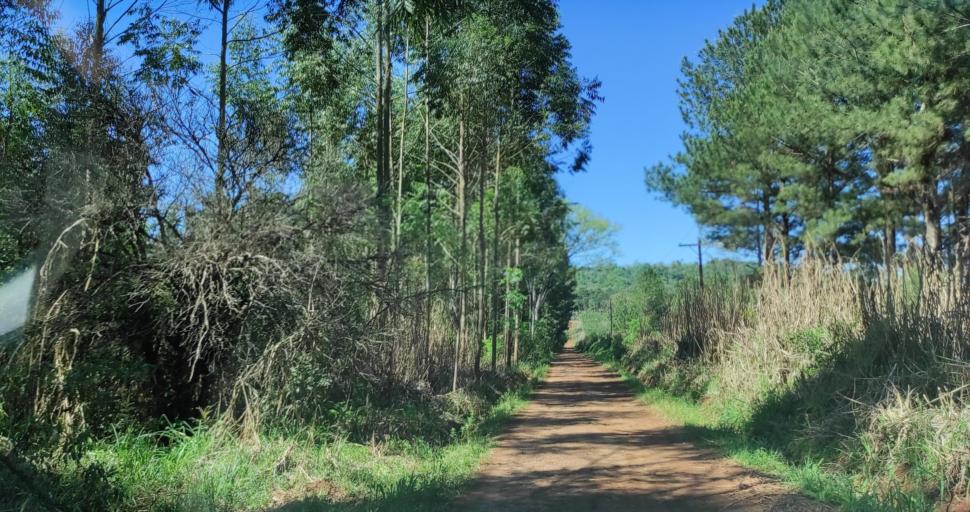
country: AR
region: Misiones
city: Capiovi
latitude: -26.9346
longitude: -55.0002
